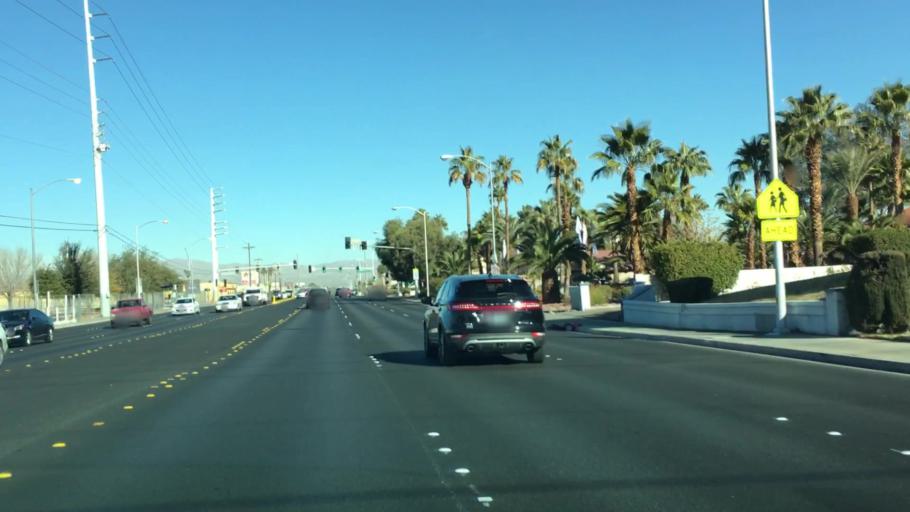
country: US
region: Nevada
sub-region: Clark County
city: Winchester
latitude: 36.1094
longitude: -115.1191
